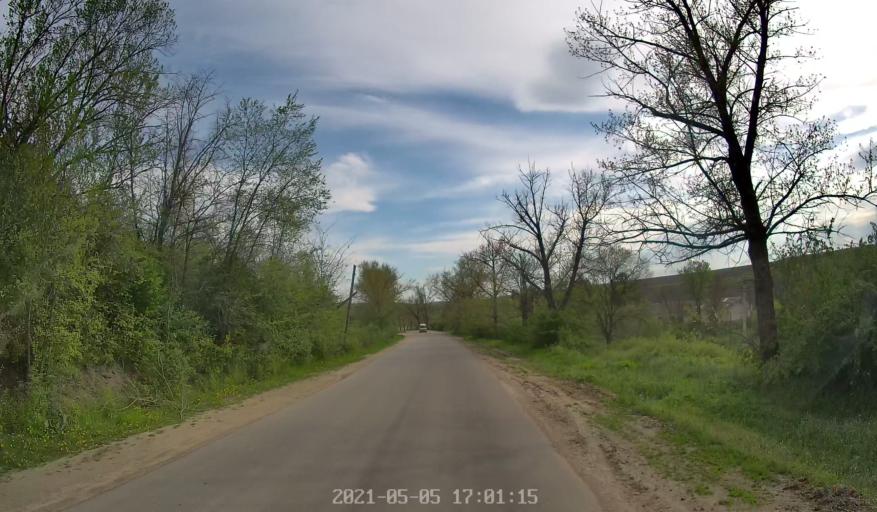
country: MD
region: Chisinau
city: Vadul lui Voda
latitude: 47.0595
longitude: 29.1326
